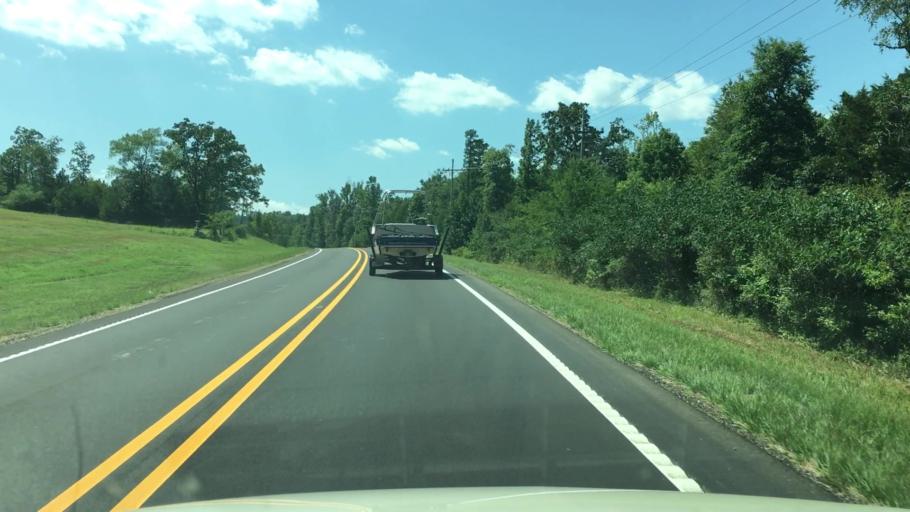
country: US
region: Arkansas
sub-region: Garland County
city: Piney
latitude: 34.5154
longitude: -93.2865
